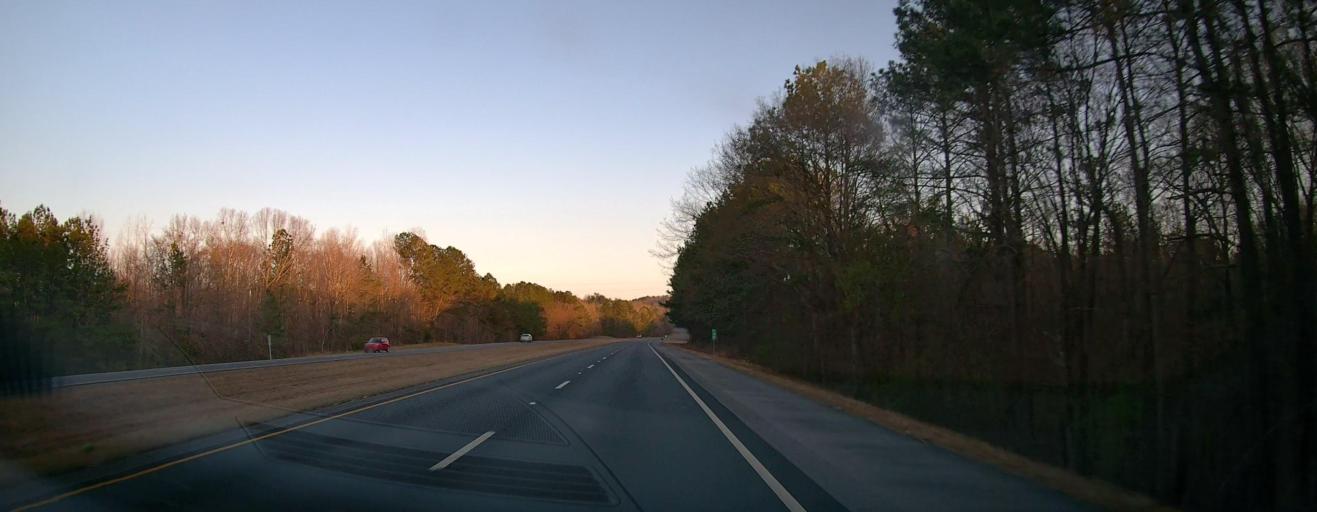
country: US
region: Alabama
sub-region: Coosa County
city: Stewartville
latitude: 33.0885
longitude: -86.2052
